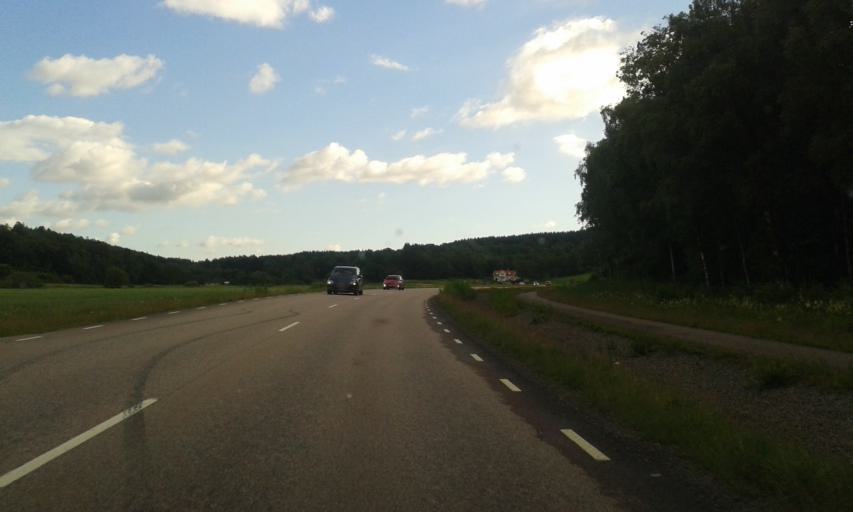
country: SE
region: Vaestra Goetaland
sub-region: Kungalvs Kommun
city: Diserod
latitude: 57.9130
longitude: 12.0158
